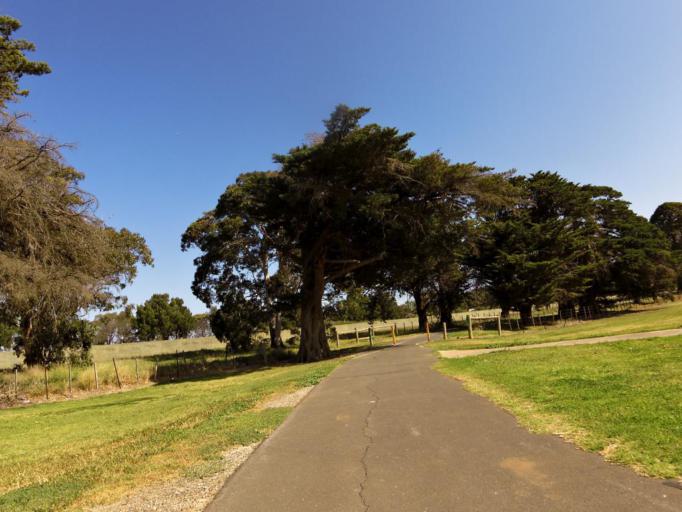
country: AU
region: Victoria
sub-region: Wyndham
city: Werribee
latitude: -37.9126
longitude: 144.6766
